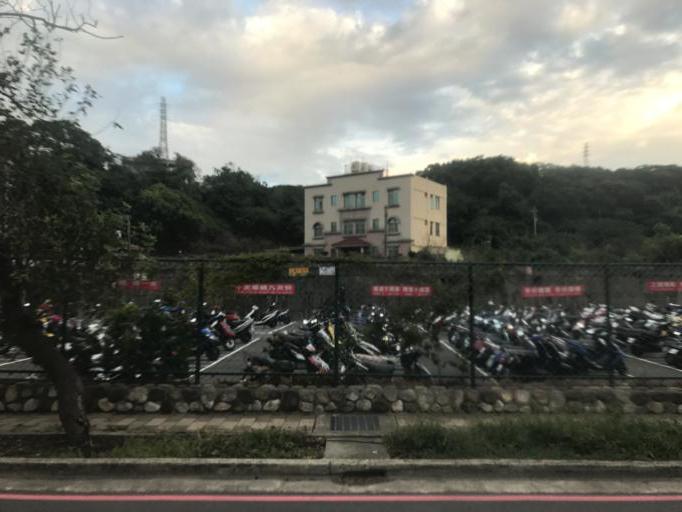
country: TW
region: Taiwan
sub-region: Hsinchu
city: Hsinchu
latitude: 24.7781
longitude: 120.9402
